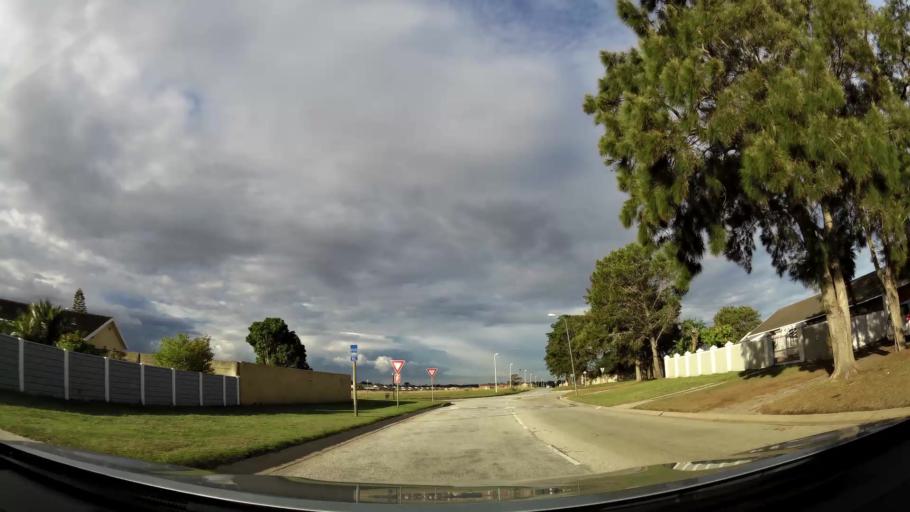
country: ZA
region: Eastern Cape
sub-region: Nelson Mandela Bay Metropolitan Municipality
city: Port Elizabeth
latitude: -33.9536
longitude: 25.4830
